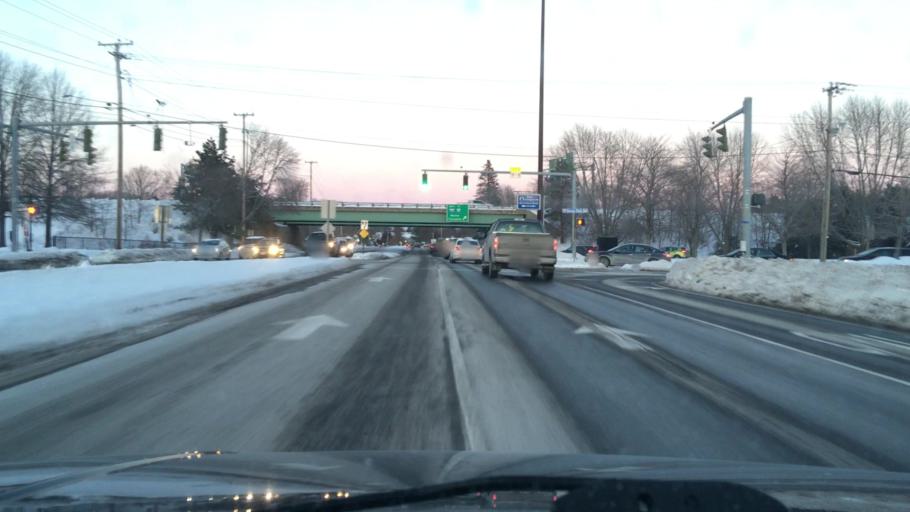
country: US
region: Maine
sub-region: York County
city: Saco
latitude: 43.5109
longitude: -70.4331
